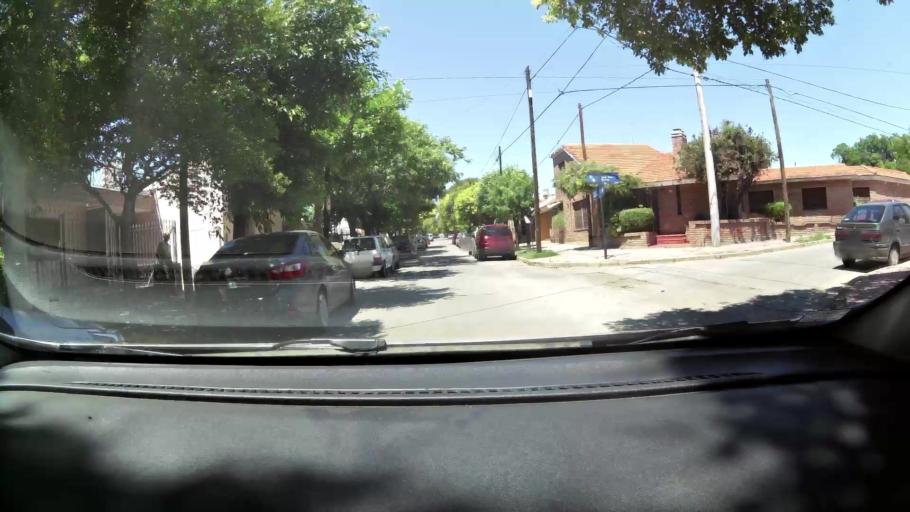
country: AR
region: Cordoba
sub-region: Departamento de Capital
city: Cordoba
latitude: -31.4117
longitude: -64.2171
